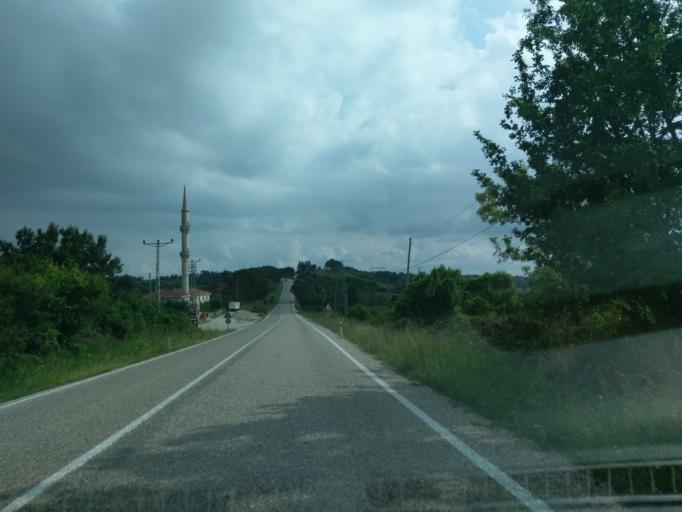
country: TR
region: Sinop
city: Erfelek
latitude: 41.9661
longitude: 34.8546
